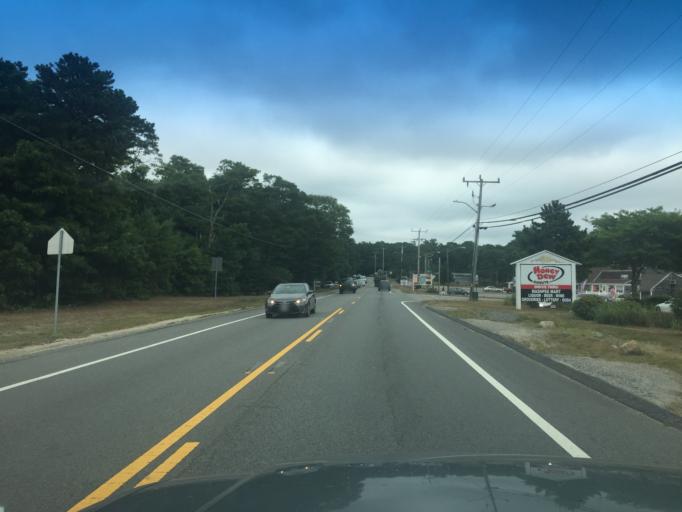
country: US
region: Massachusetts
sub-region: Barnstable County
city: Mashpee
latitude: 41.6341
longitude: -70.4593
